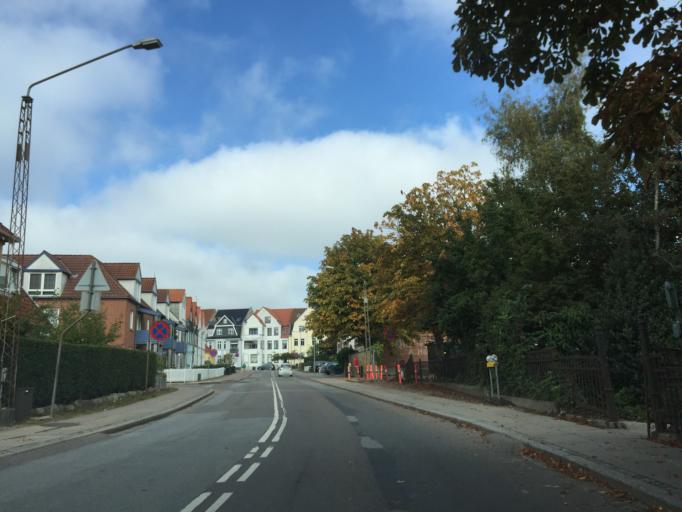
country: DK
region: South Denmark
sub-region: Sonderborg Kommune
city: Sonderborg
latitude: 54.9126
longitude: 9.7980
